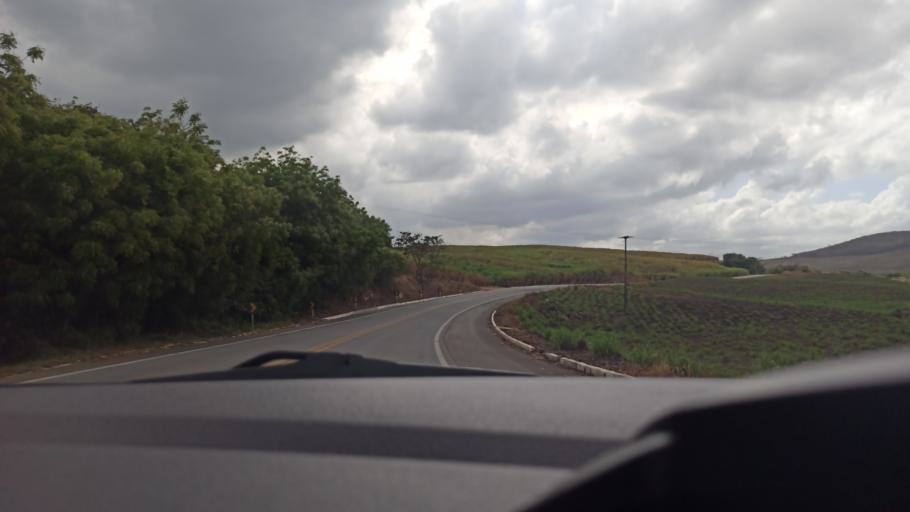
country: BR
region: Pernambuco
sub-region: Timbauba
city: Timbauba
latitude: -7.5403
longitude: -35.2772
